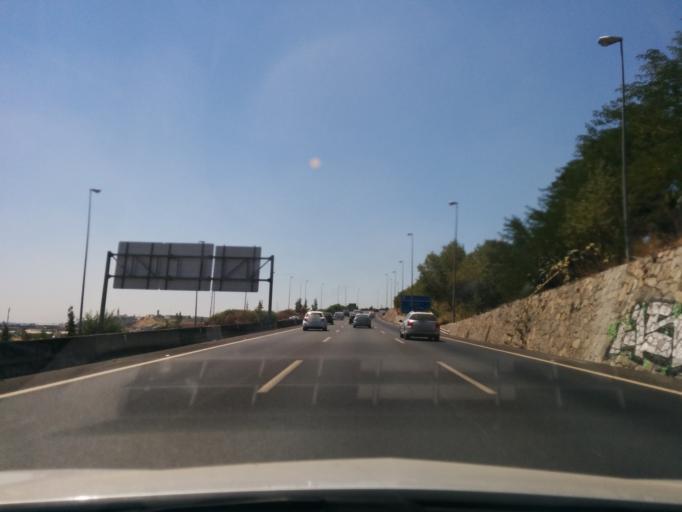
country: ES
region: Andalusia
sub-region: Provincia de Sevilla
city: Camas
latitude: 37.3858
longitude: -6.0343
